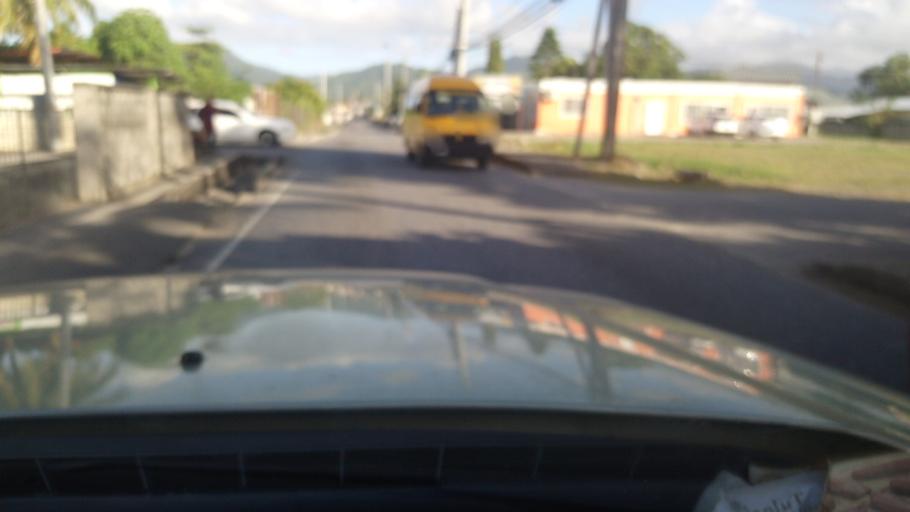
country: TT
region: Borough of Arima
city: Arima
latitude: 10.6253
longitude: -61.2737
